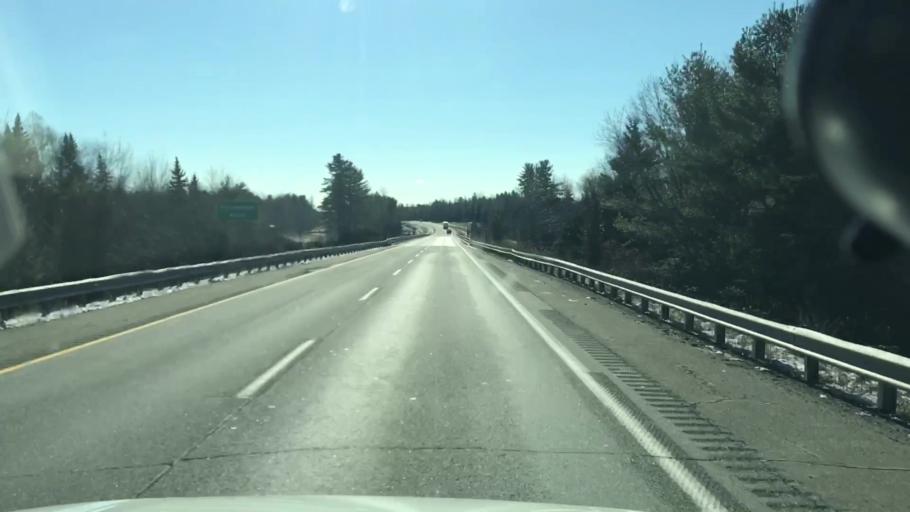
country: US
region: Maine
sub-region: Penobscot County
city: Howland
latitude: 45.2672
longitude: -68.6801
